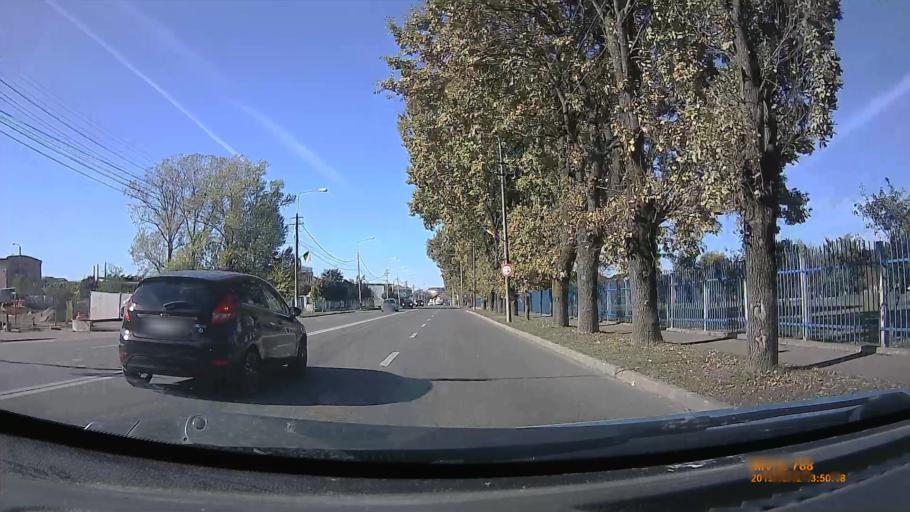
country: RO
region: Bihor
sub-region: Comuna Sanmartin
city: Sanmartin
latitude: 47.0422
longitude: 21.9740
